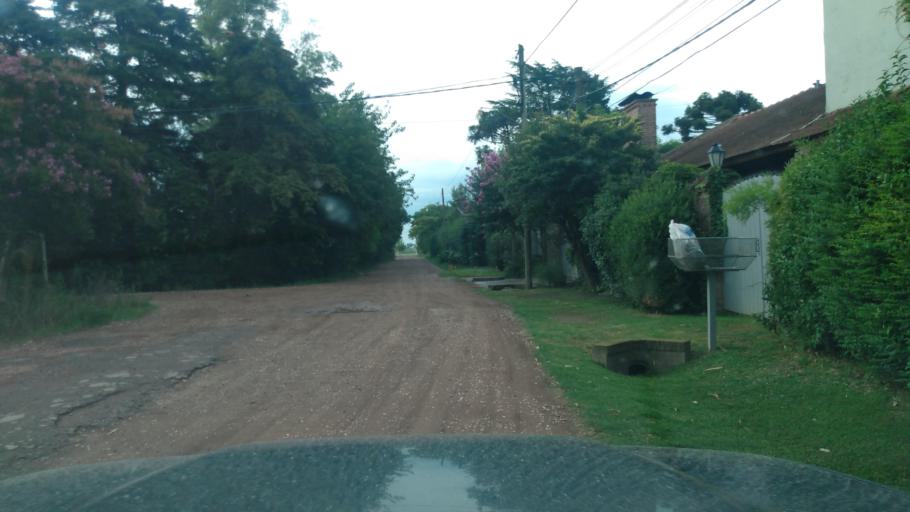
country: AR
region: Buenos Aires
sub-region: Partido de Lujan
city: Lujan
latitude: -34.5467
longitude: -59.1261
